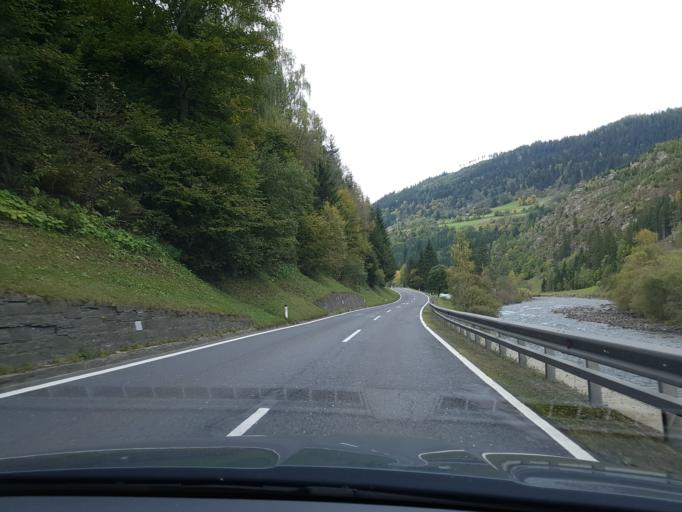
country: AT
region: Salzburg
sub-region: Politischer Bezirk Tamsweg
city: Ramingstein
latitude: 47.0735
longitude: 13.8539
